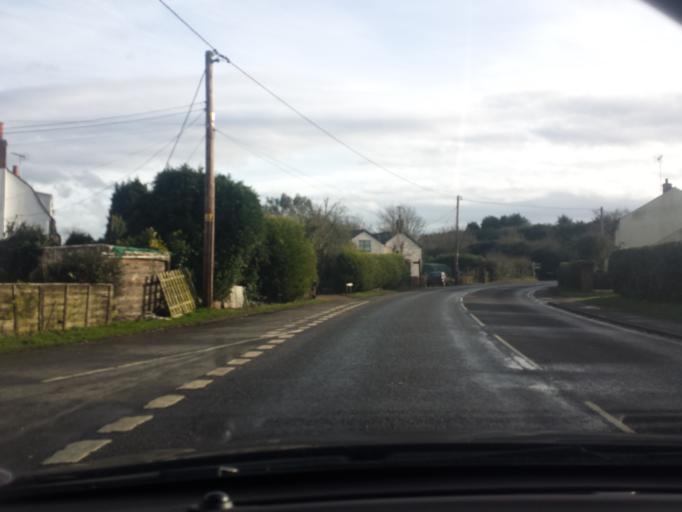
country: GB
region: England
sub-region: Essex
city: Great Bentley
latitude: 51.8778
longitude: 1.0374
